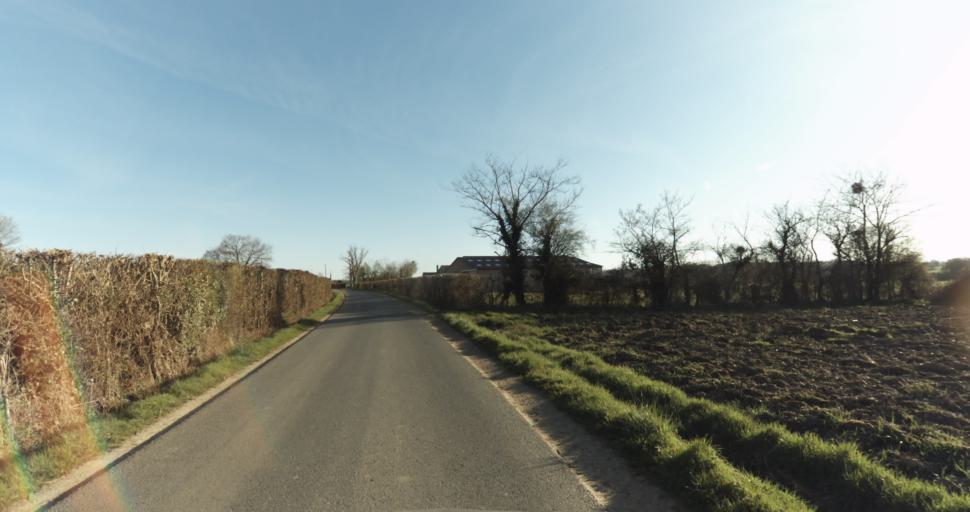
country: FR
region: Lower Normandy
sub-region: Departement de l'Orne
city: Trun
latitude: 48.9221
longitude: 0.0286
